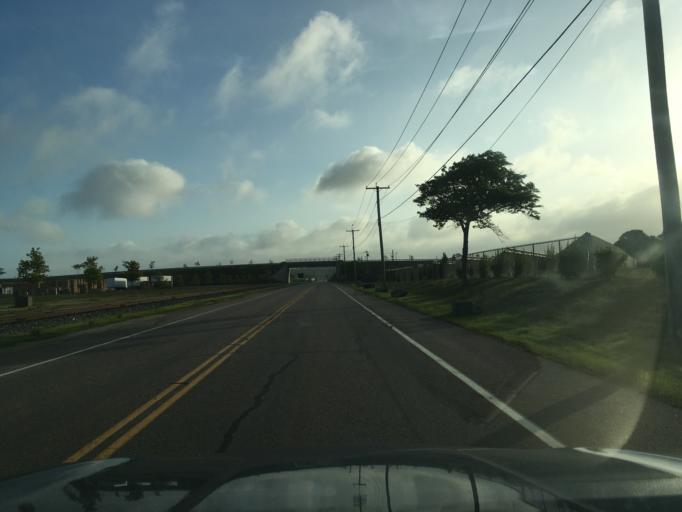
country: US
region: Rhode Island
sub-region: Kent County
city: East Greenwich
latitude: 41.6093
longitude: -71.4355
